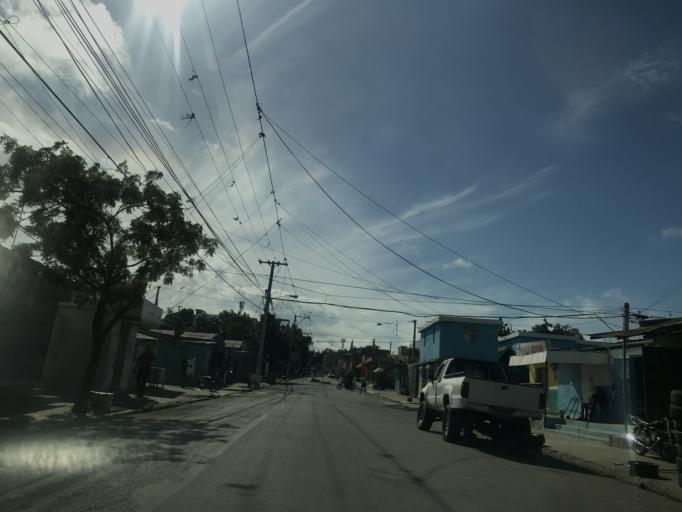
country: DO
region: Santiago
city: Palmar Arriba
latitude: 19.4815
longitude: -70.7492
